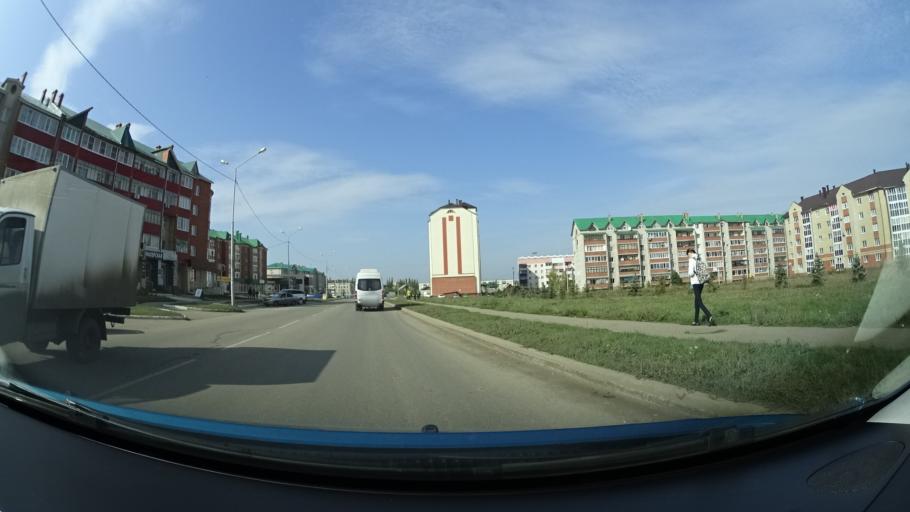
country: RU
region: Bashkortostan
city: Tuymazy
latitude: 54.5971
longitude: 53.7118
